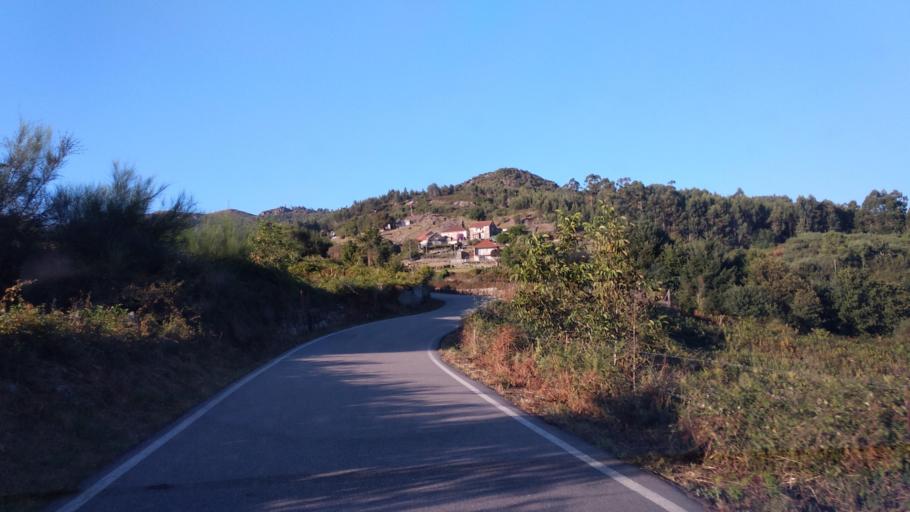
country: ES
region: Galicia
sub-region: Provincia de Pontevedra
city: Ponte Caldelas
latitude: 42.3561
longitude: -8.4911
